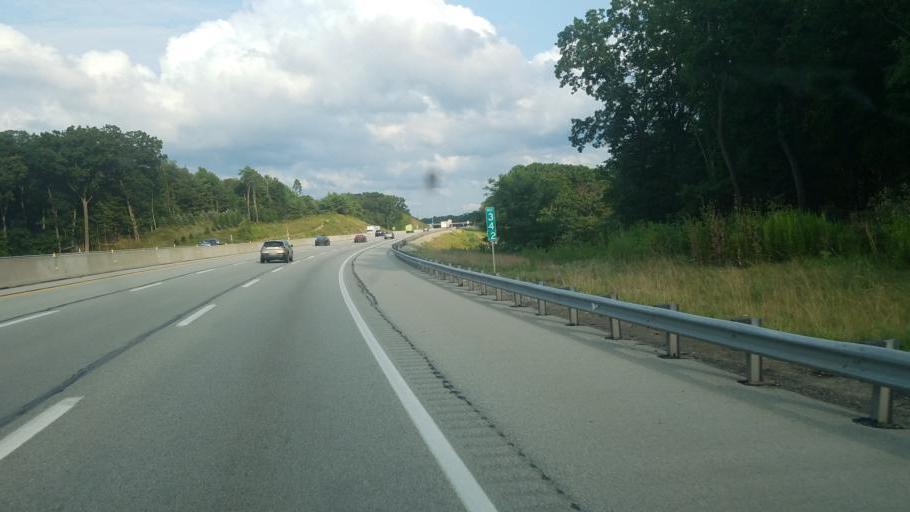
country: US
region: Pennsylvania
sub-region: Allegheny County
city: Gibsonia
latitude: 40.6440
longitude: -80.0169
